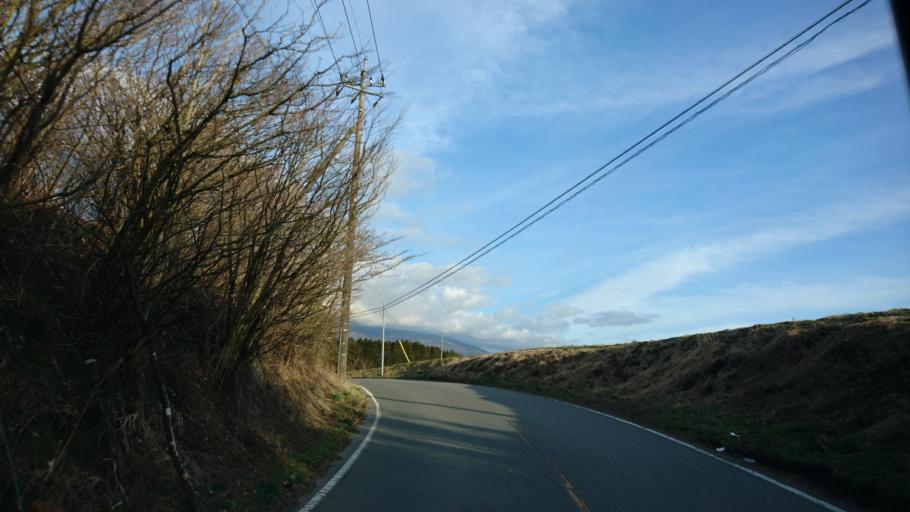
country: JP
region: Yamanashi
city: Fujikawaguchiko
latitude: 35.3901
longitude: 138.5940
